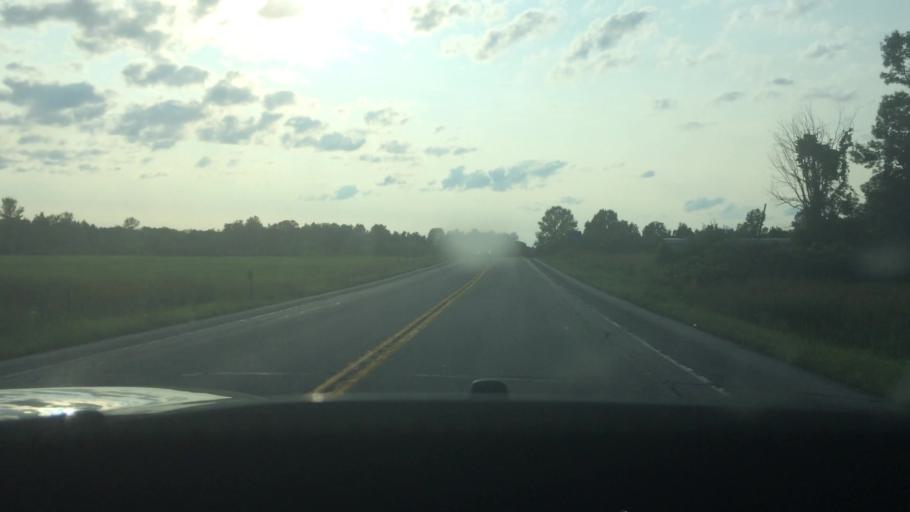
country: US
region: New York
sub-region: St. Lawrence County
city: Ogdensburg
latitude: 44.6722
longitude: -75.3904
